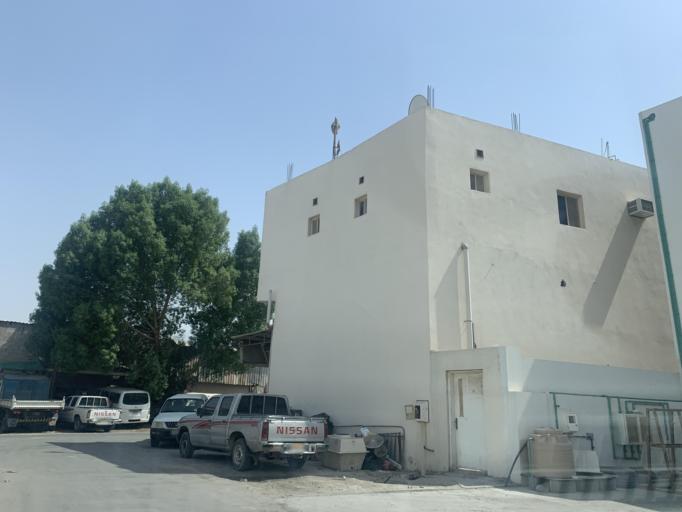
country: BH
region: Central Governorate
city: Madinat Hamad
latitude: 26.1377
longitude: 50.4850
